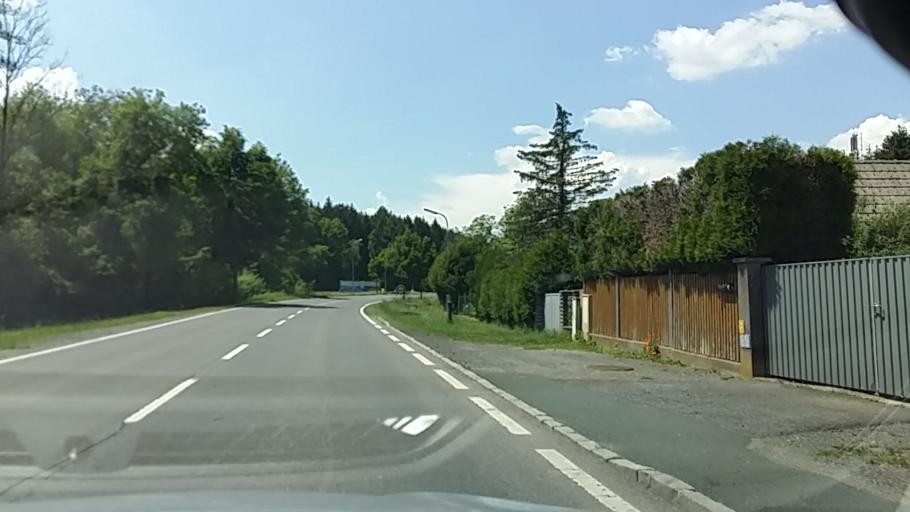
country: AT
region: Burgenland
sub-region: Politischer Bezirk Oberpullendorf
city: Pilgersdorf
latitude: 47.4011
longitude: 16.3710
